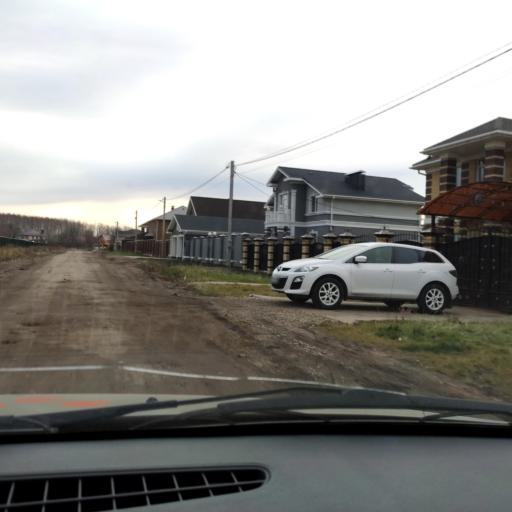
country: RU
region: Bashkortostan
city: Ufa
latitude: 54.6643
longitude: 55.9197
